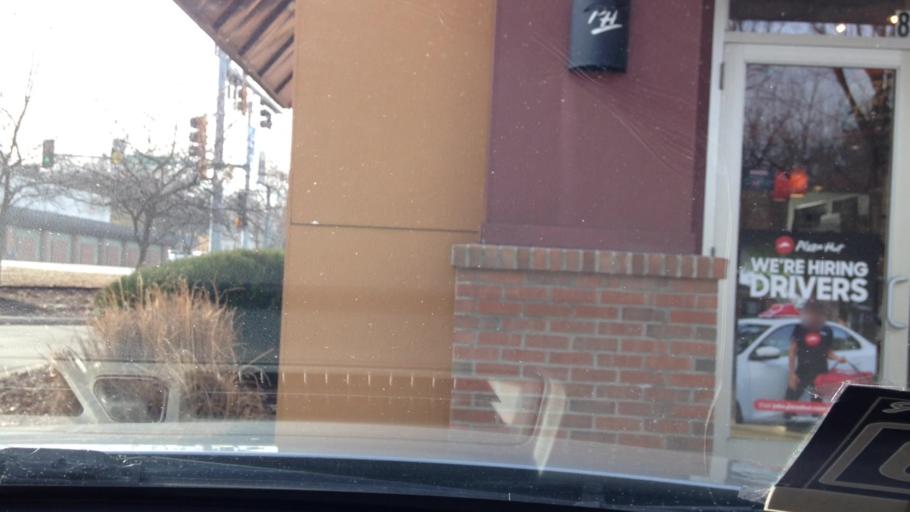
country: US
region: Kansas
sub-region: Leavenworth County
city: Leavenworth
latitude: 39.3111
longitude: -94.9118
